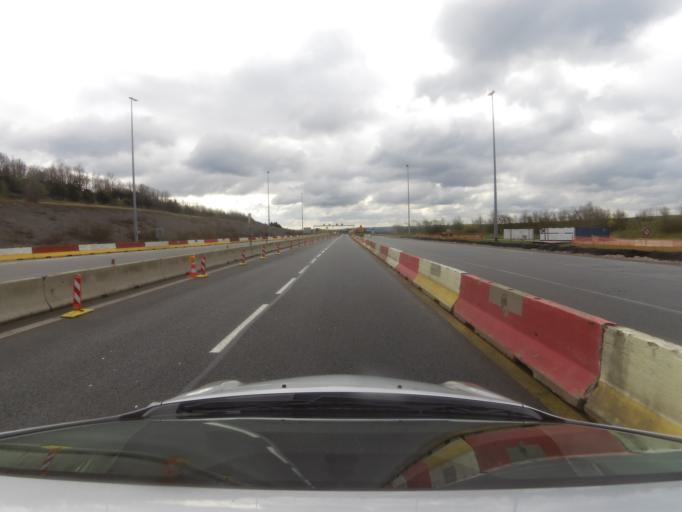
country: FR
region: Nord-Pas-de-Calais
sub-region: Departement du Pas-de-Calais
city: Saint-Etienne-au-Mont
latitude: 50.6879
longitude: 1.6427
